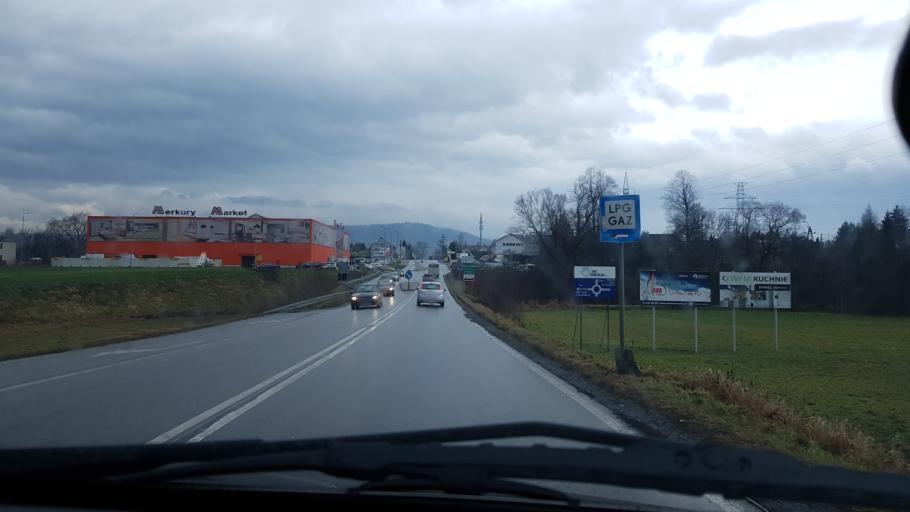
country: PL
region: Silesian Voivodeship
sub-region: Powiat zywiecki
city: Zywiec
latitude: 49.6951
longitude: 19.1805
